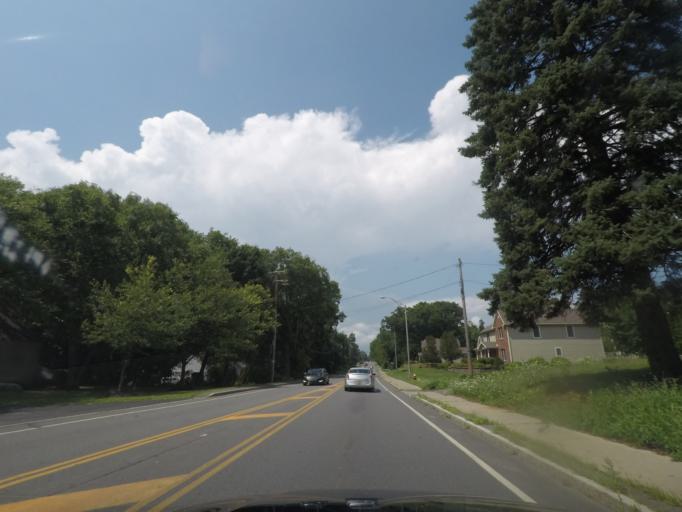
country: US
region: New York
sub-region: Albany County
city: West Albany
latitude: 42.7084
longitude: -73.7787
